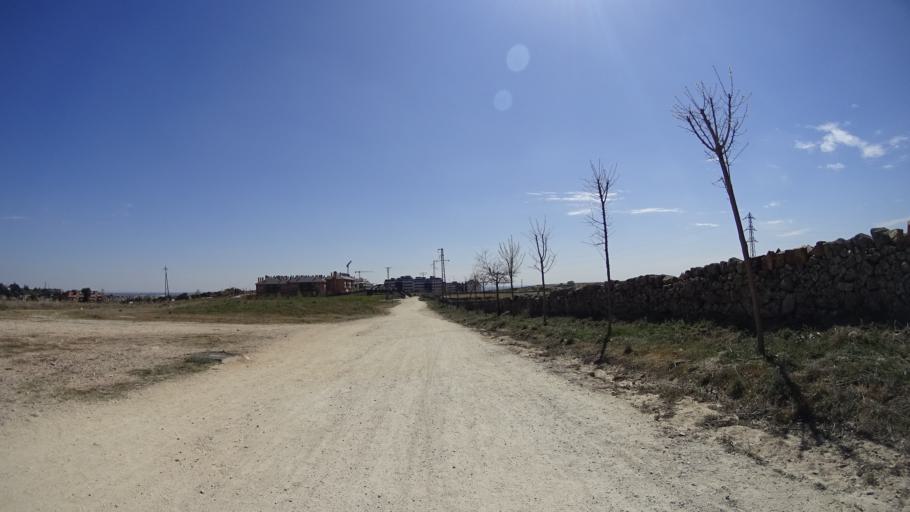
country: ES
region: Madrid
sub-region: Provincia de Madrid
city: Colmenar Viejo
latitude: 40.6549
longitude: -3.7902
